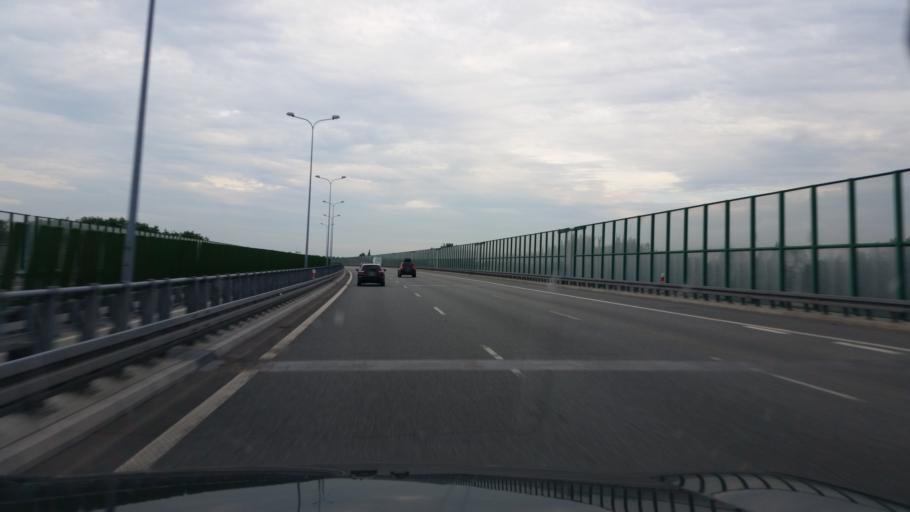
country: PL
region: Silesian Voivodeship
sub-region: Powiat gliwicki
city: Knurow
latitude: 50.2204
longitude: 18.6917
